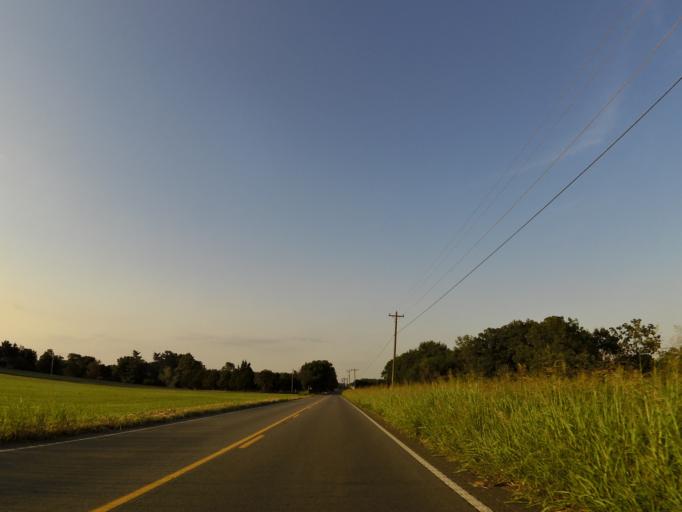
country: US
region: Tennessee
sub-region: Monroe County
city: Sweetwater
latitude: 35.5554
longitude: -84.5113
